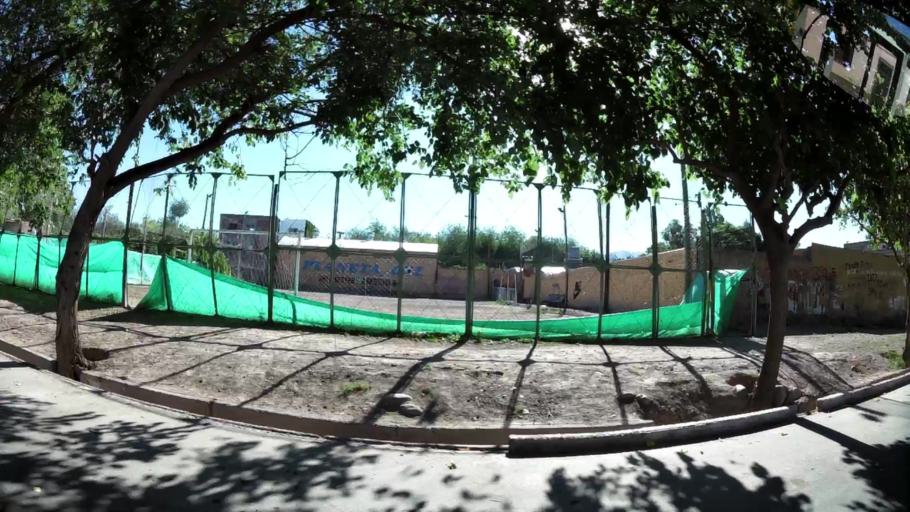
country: AR
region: Mendoza
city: Las Heras
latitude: -32.8443
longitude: -68.8329
